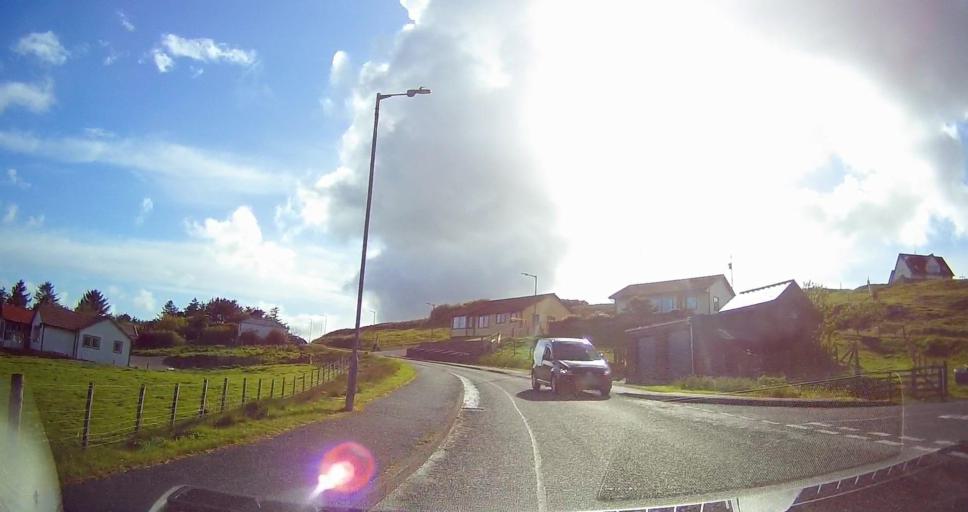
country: GB
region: Scotland
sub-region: Shetland Islands
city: Shetland
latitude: 60.3700
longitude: -1.1339
